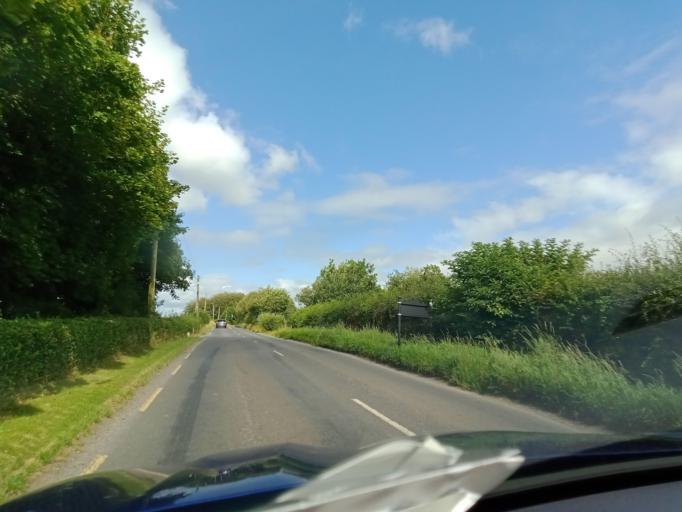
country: IE
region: Leinster
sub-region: Laois
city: Abbeyleix
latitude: 52.9548
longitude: -7.3016
